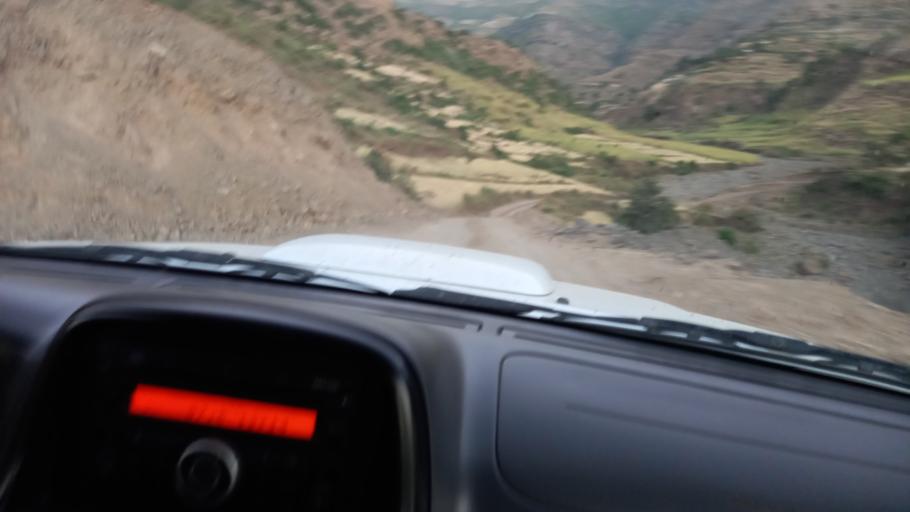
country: ET
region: Amhara
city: Debark'
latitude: 13.0305
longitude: 38.0547
